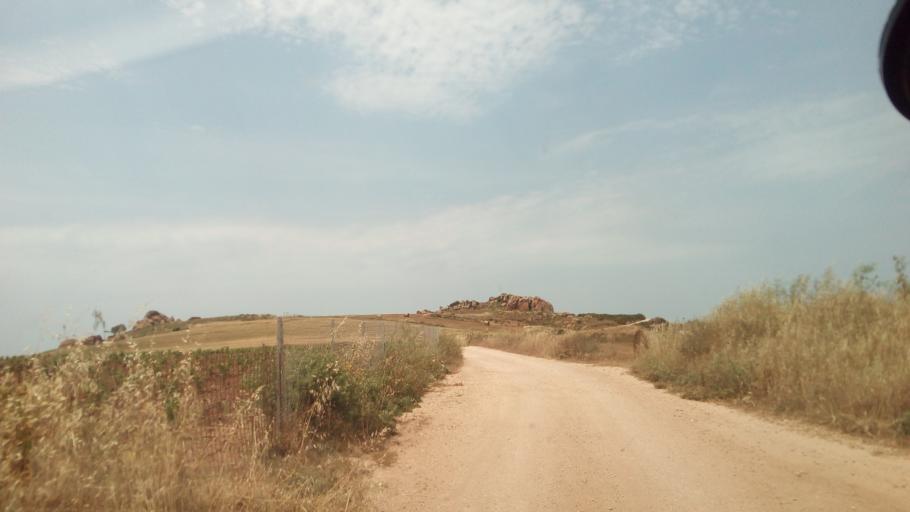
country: CY
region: Pafos
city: Polis
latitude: 34.9801
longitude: 32.3567
